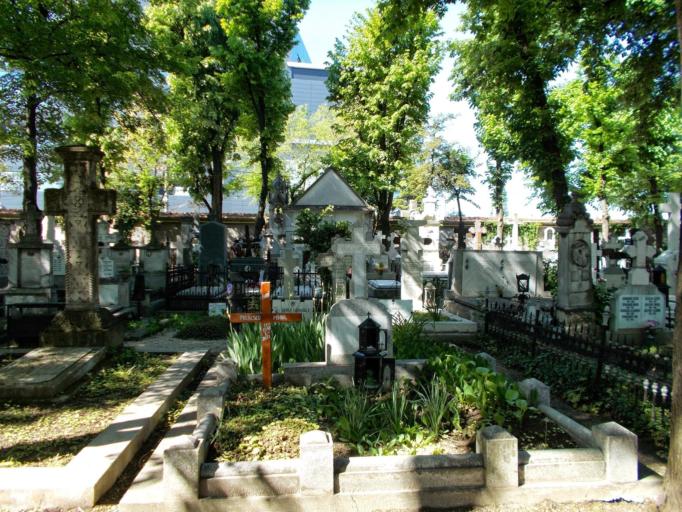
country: RO
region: Bucuresti
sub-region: Municipiul Bucuresti
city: Bucuresti
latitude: 44.4023
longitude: 26.0993
